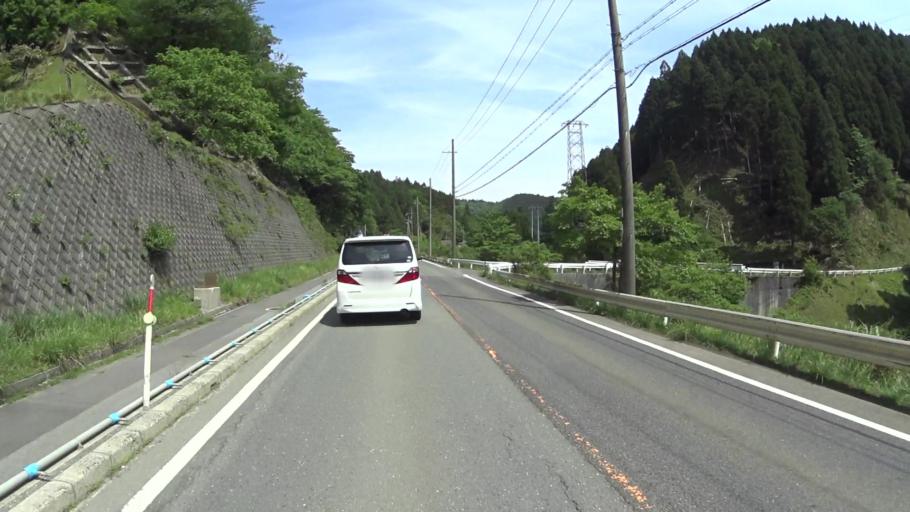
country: JP
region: Fukui
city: Obama
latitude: 35.4350
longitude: 135.9272
